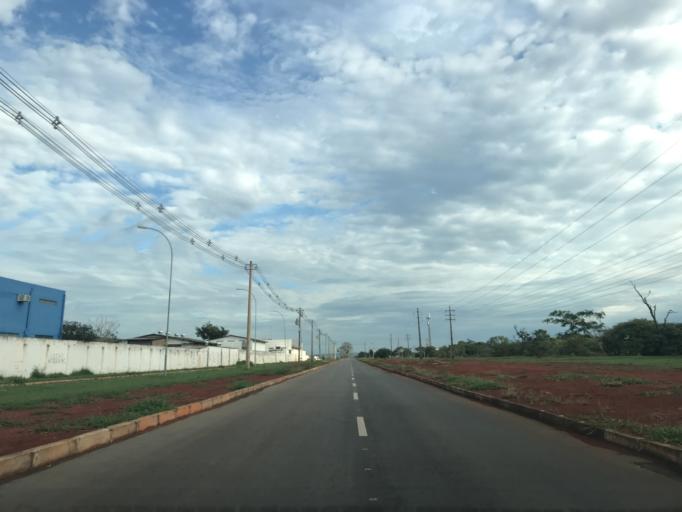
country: BR
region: Federal District
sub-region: Brasilia
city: Brasilia
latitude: -15.7793
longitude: -47.8948
